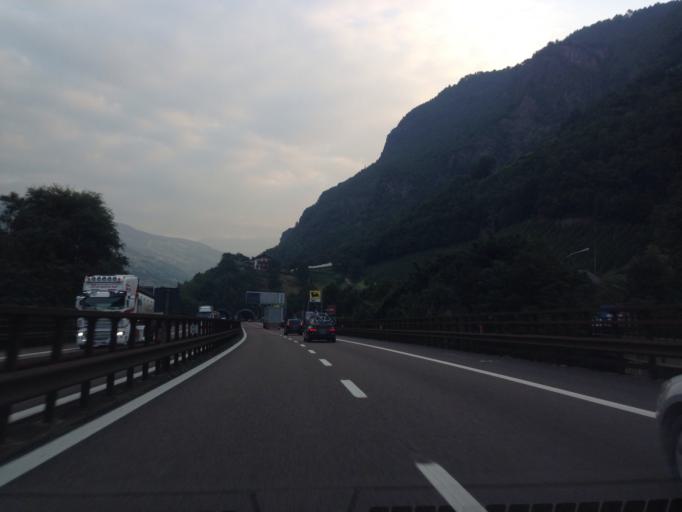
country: IT
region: Trentino-Alto Adige
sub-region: Bolzano
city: Ponte Gardena
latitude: 46.5686
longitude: 11.5222
